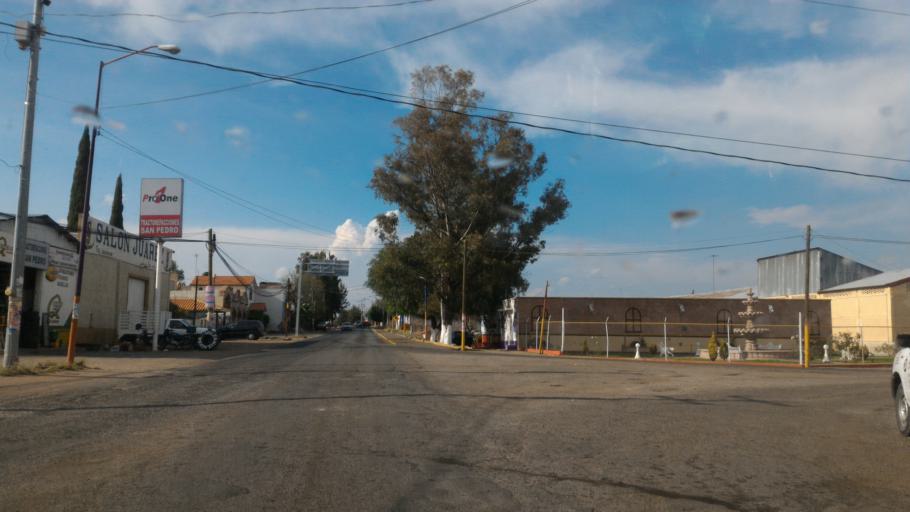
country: MX
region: Guanajuato
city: Ciudad Manuel Doblado
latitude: 20.7339
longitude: -101.9518
